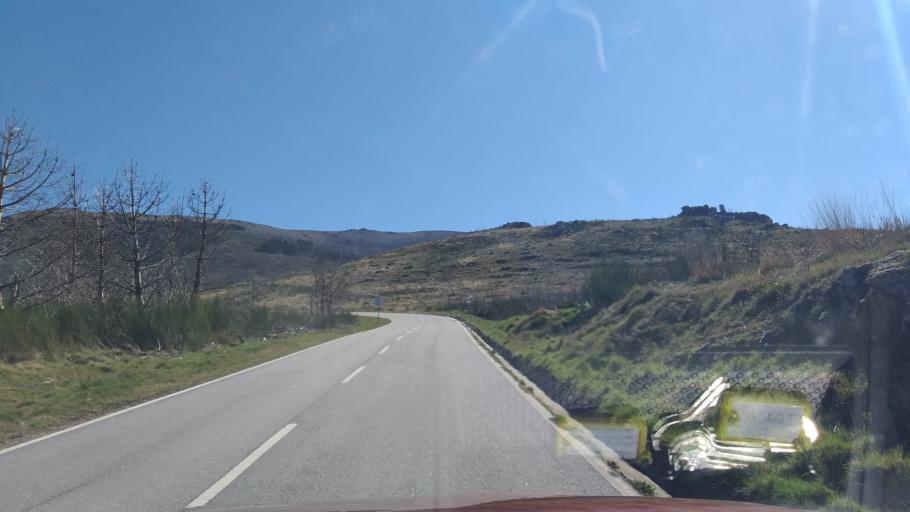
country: PT
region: Guarda
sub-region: Manteigas
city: Manteigas
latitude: 40.4888
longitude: -7.5662
